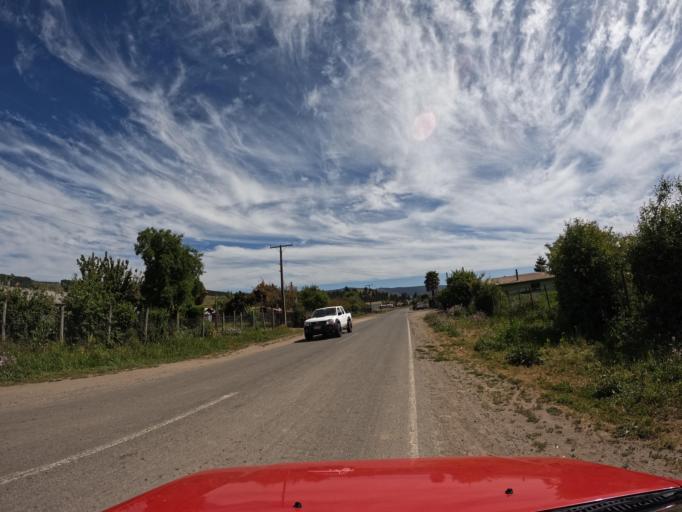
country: CL
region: Maule
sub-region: Provincia de Talca
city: Constitucion
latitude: -35.0261
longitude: -72.0461
